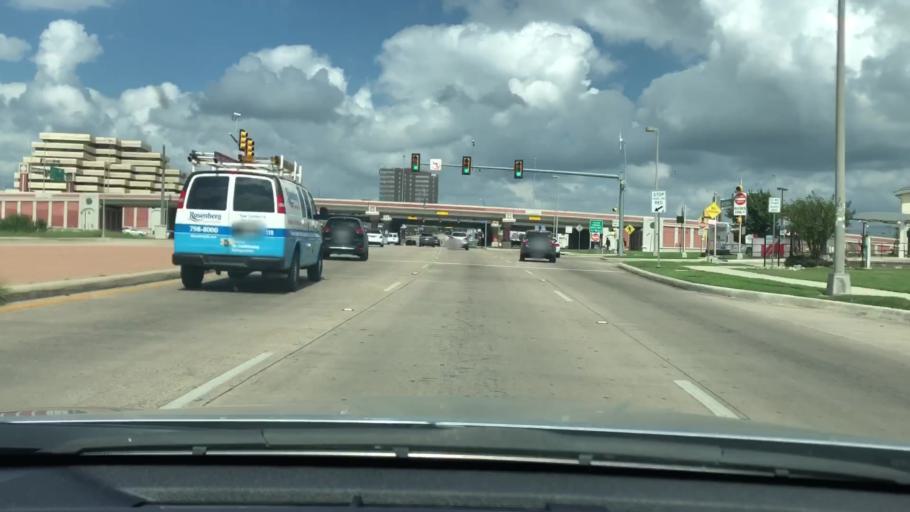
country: US
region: Texas
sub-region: Bexar County
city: Castle Hills
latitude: 29.5184
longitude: -98.4991
